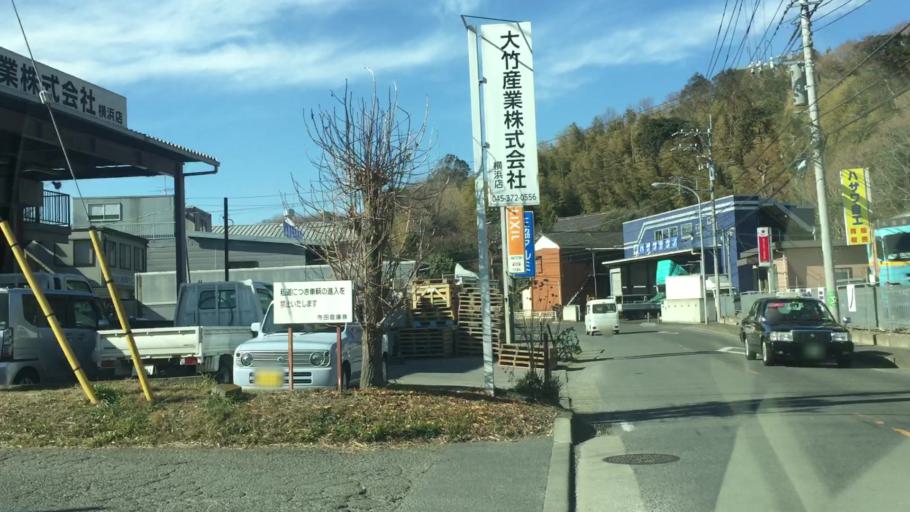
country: JP
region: Kanagawa
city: Yokohama
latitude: 35.4867
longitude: 139.5870
